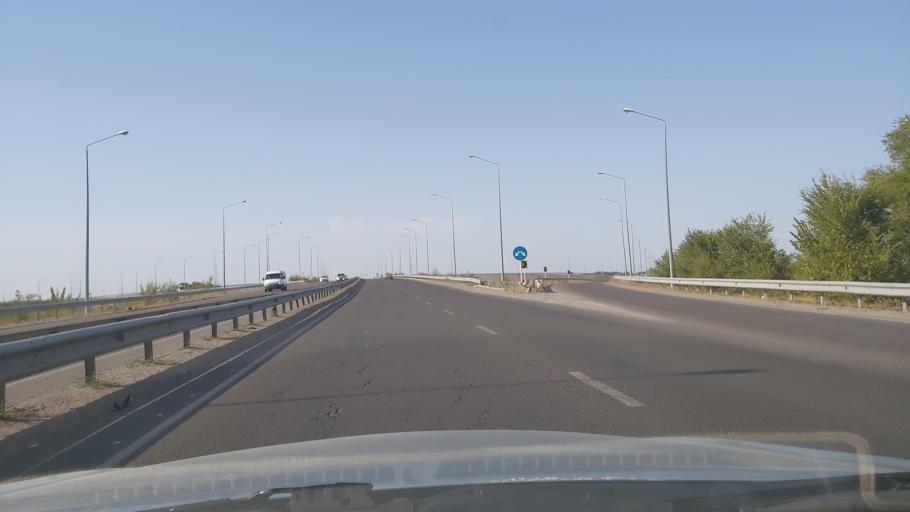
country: KZ
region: Almaty Oblysy
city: Energeticheskiy
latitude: 43.4643
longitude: 77.0332
